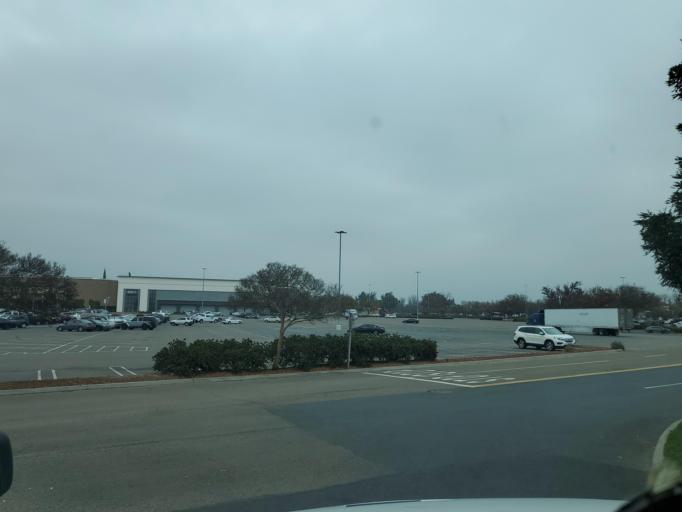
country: US
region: California
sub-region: Stanislaus County
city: Salida
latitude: 37.6861
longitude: -121.0521
